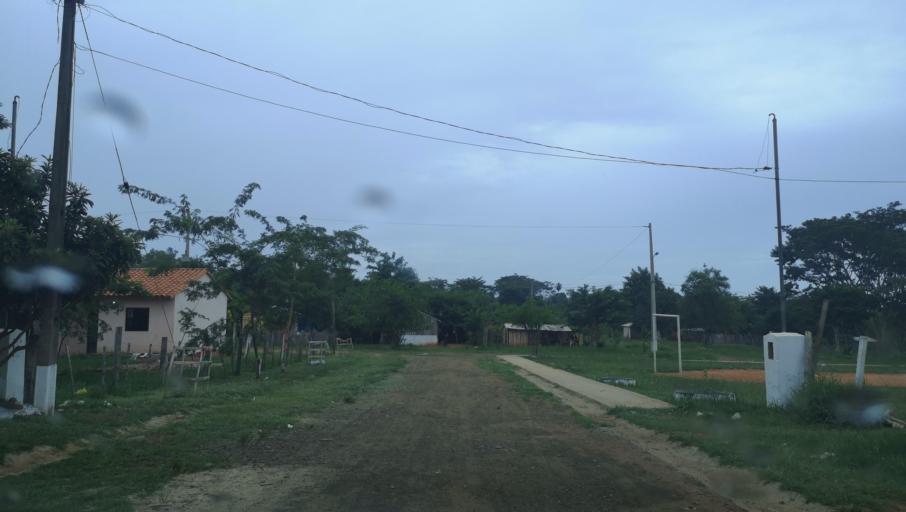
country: PY
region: San Pedro
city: Capiibary
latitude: -24.7258
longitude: -56.0094
